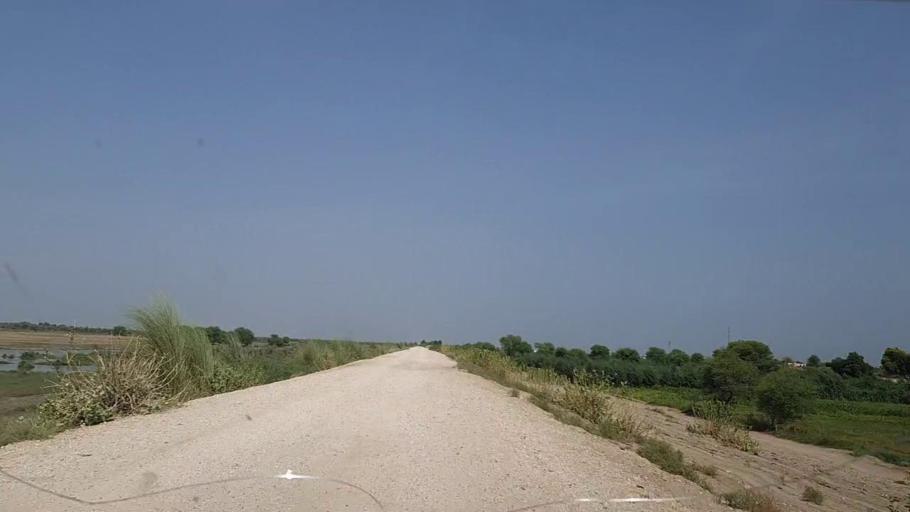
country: PK
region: Sindh
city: Ghotki
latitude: 28.1169
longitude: 69.3652
